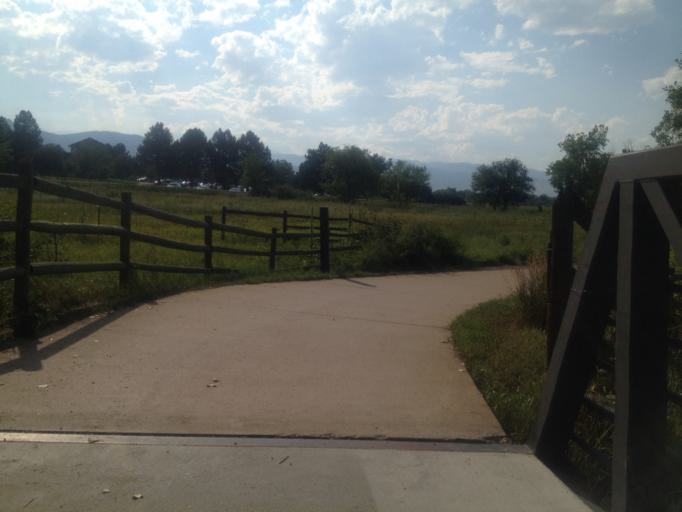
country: US
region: Colorado
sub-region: Boulder County
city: Boulder
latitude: 39.9923
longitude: -105.2176
